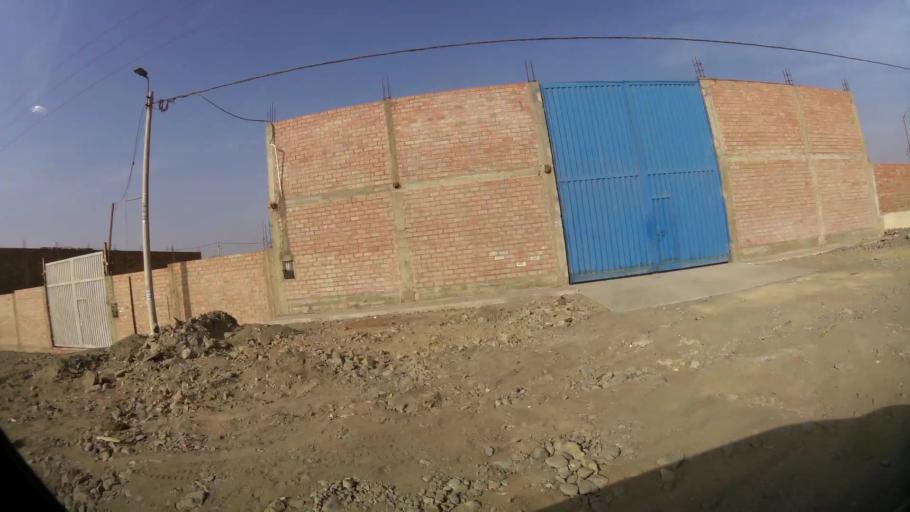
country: PE
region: Lima
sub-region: Lima
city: Santa Rosa
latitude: -11.7541
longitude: -77.1608
